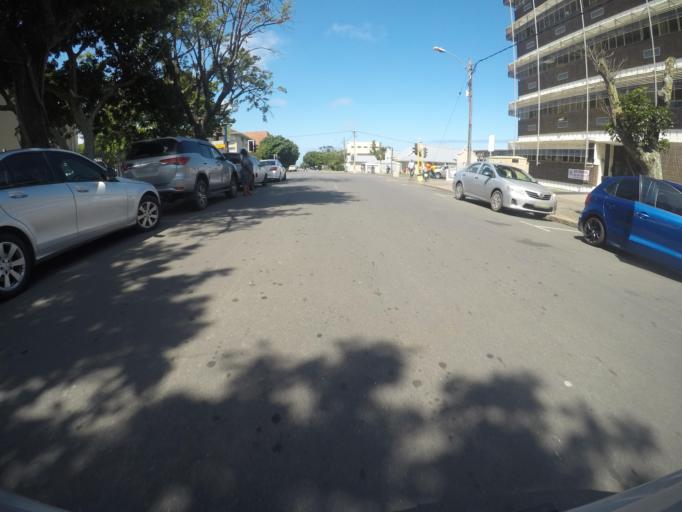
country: ZA
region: Eastern Cape
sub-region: Buffalo City Metropolitan Municipality
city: East London
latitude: -33.0019
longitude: 27.8988
